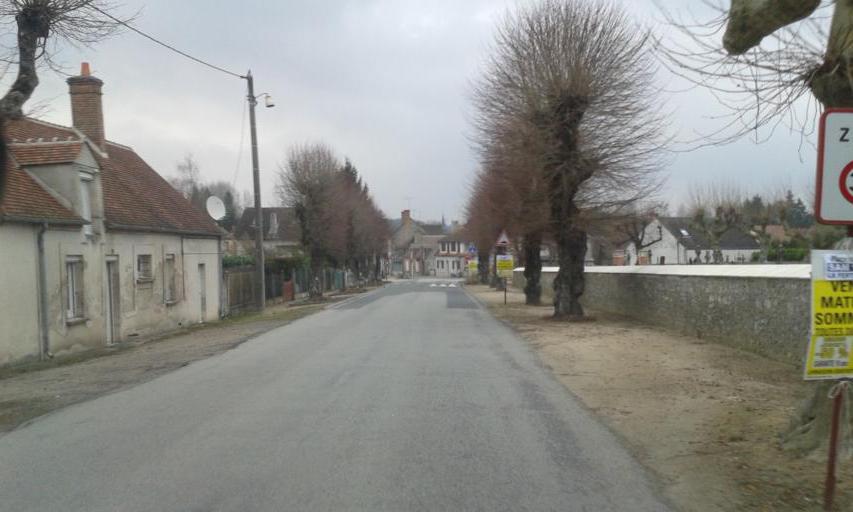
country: FR
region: Centre
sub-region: Departement du Loir-et-Cher
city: Dhuizon
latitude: 47.6517
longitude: 1.6710
